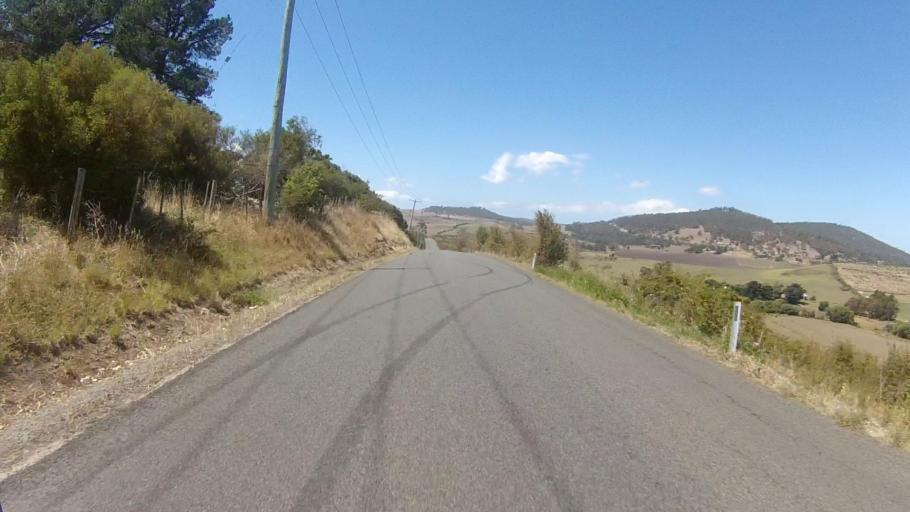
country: AU
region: Tasmania
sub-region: Sorell
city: Sorell
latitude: -42.7728
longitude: 147.5854
